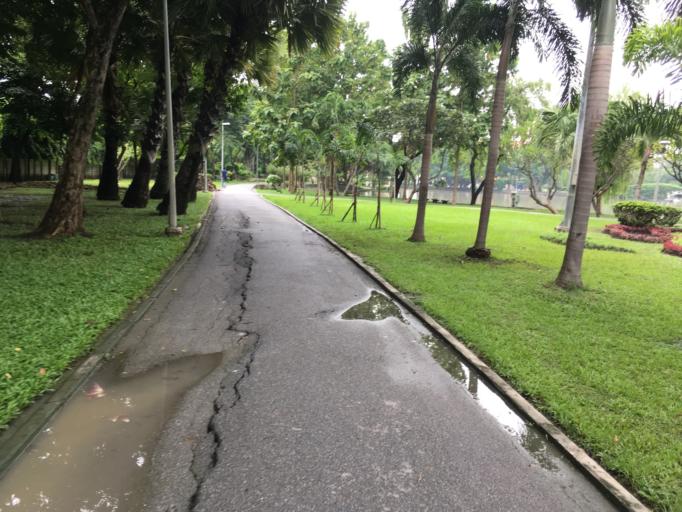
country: TH
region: Bangkok
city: Bueng Kum
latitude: 13.7854
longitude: 100.6708
